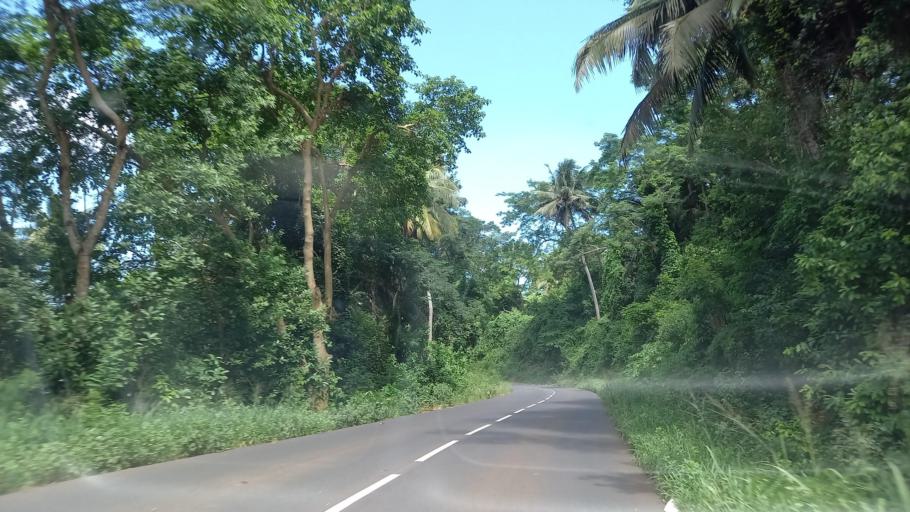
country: YT
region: Acoua
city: Acoua
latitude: -12.7461
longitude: 45.0554
